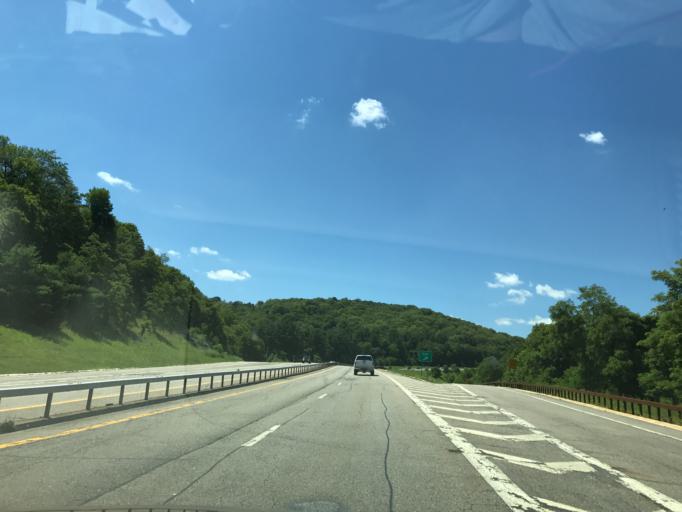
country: US
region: New York
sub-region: Dutchess County
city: Brinckerhoff
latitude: 41.5149
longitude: -73.7868
